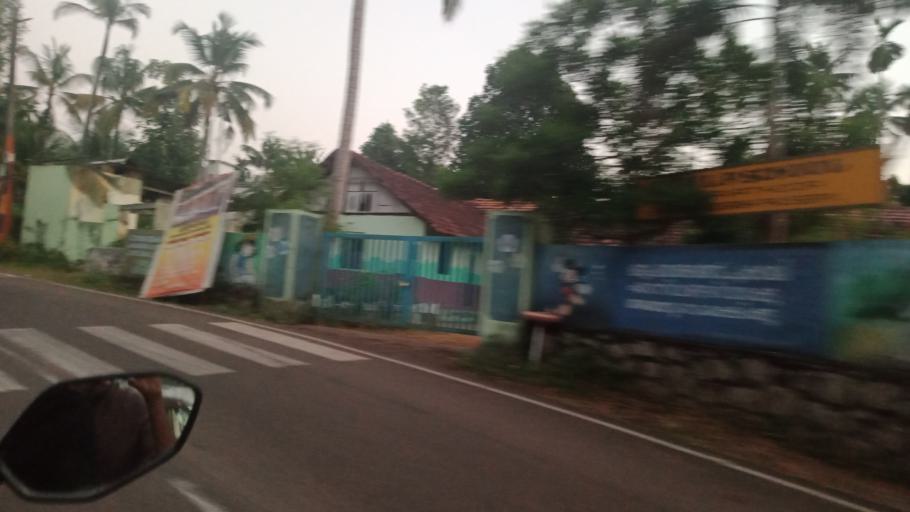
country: IN
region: Kerala
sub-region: Ernakulam
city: Angamali
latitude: 10.2005
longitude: 76.3034
